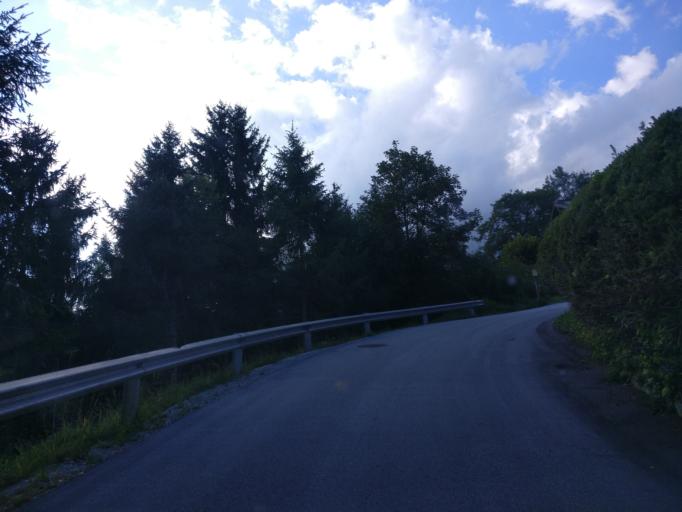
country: AT
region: Salzburg
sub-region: Politischer Bezirk Sankt Johann im Pongau
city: Muhlbach am Hochkonig
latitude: 47.3786
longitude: 13.1265
